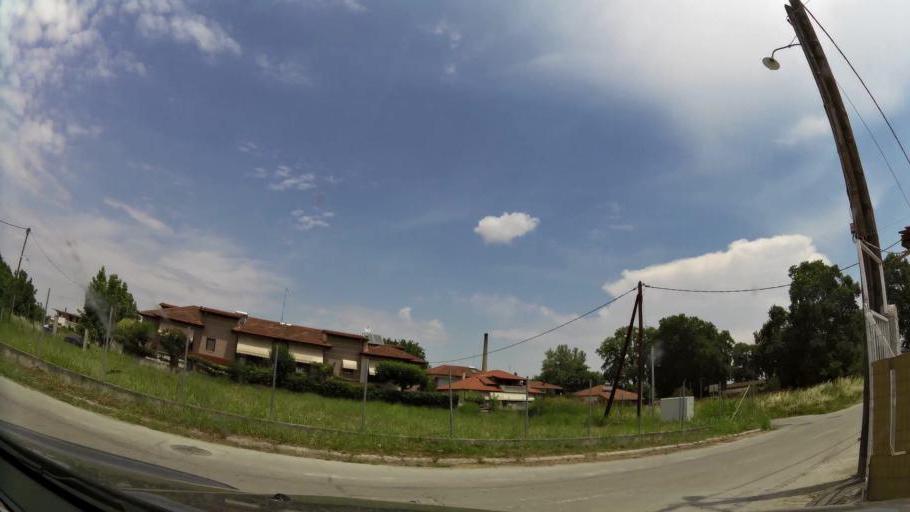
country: GR
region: Central Macedonia
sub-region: Nomos Pierias
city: Peristasi
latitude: 40.2662
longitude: 22.5286
